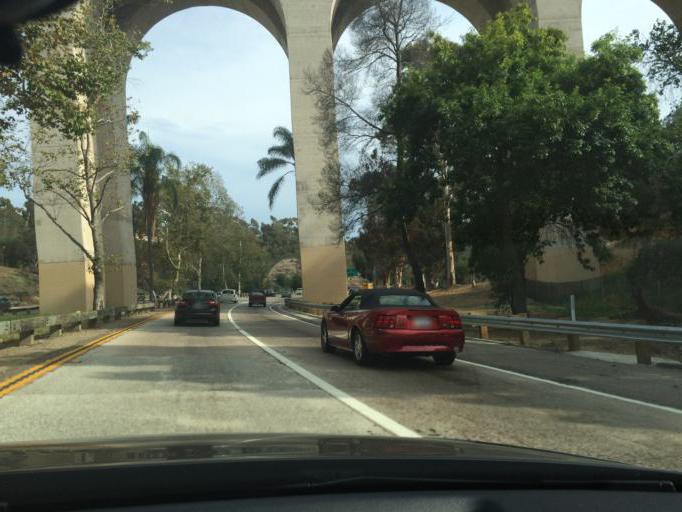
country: US
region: California
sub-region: San Diego County
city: San Diego
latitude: 32.7321
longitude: -117.1548
